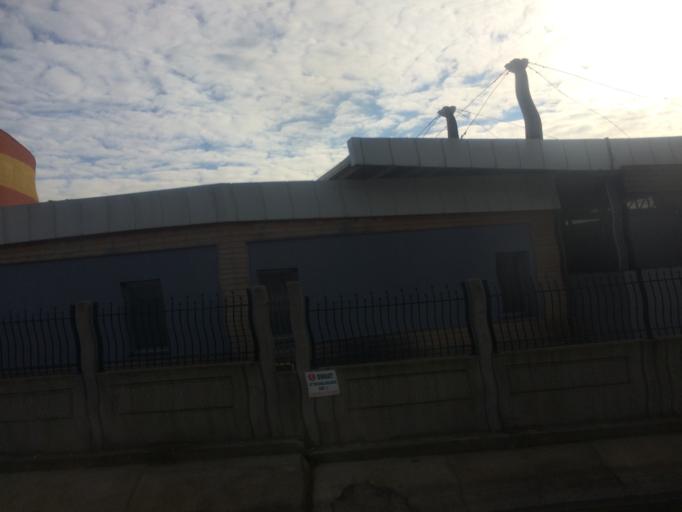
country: TR
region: Izmir
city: Karsiyaka
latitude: 38.4945
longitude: 26.9568
